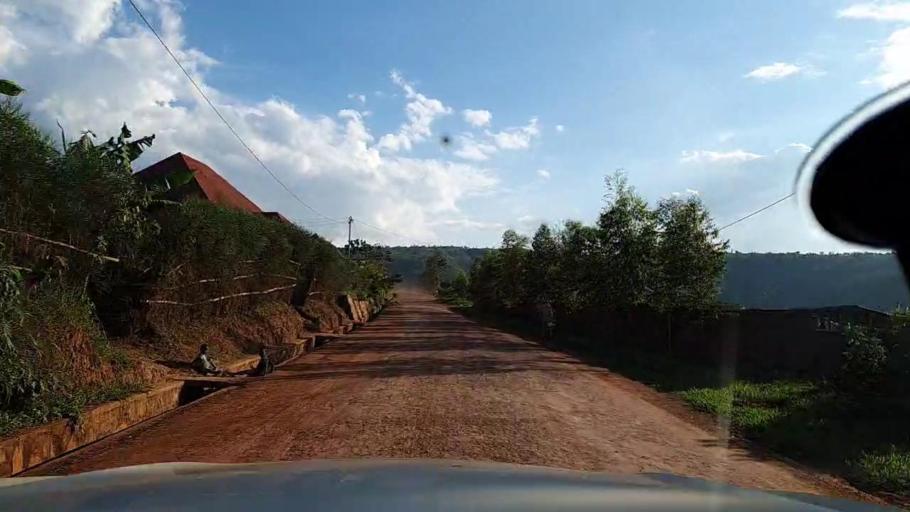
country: RW
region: Kigali
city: Kigali
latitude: -1.8994
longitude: 29.9645
